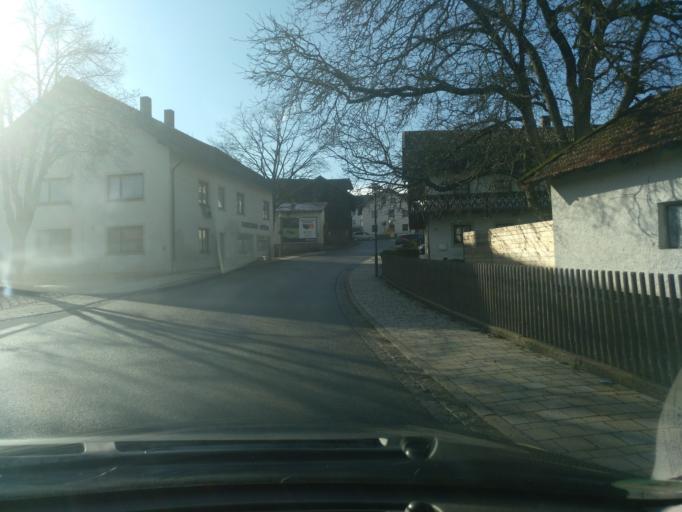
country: DE
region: Bavaria
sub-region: Upper Palatinate
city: Zandt
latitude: 49.1565
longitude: 12.7266
